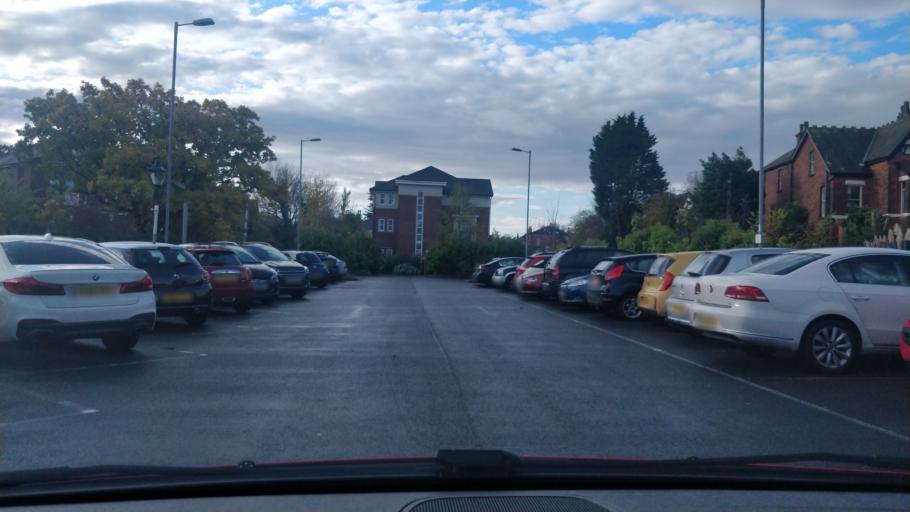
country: GB
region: England
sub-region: Sefton
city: Southport
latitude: 53.6327
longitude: -3.0154
